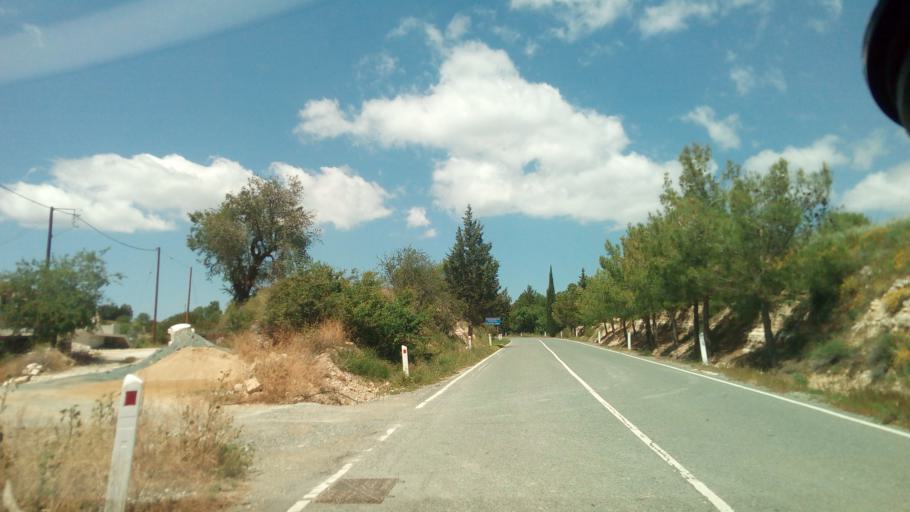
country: CY
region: Limassol
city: Pachna
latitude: 34.8349
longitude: 32.7721
